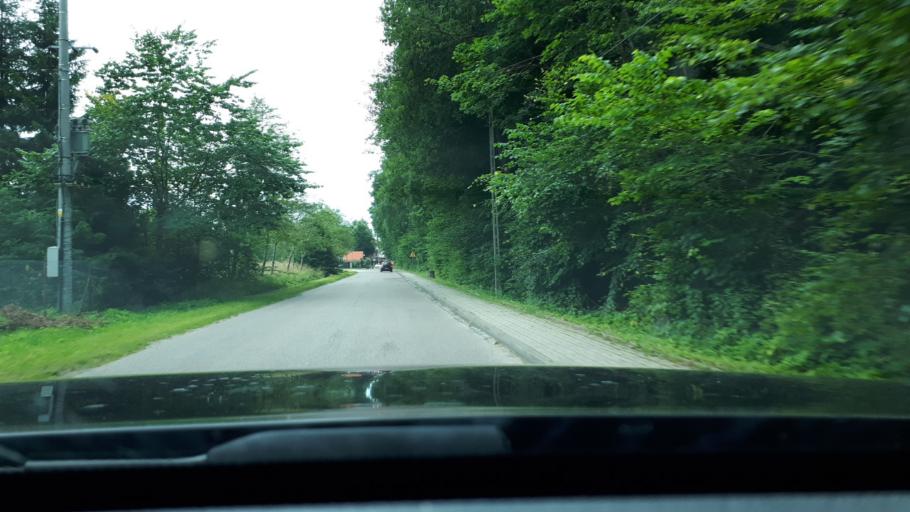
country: PL
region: Warmian-Masurian Voivodeship
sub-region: Powiat ostrodzki
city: Ostroda
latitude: 53.6906
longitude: 20.0947
